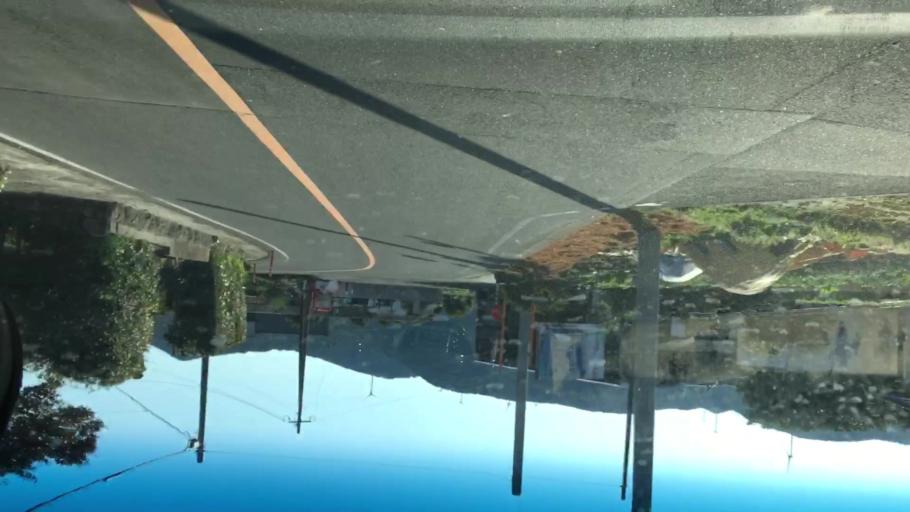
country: JP
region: Kagoshima
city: Satsumasendai
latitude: 31.8297
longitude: 130.2434
